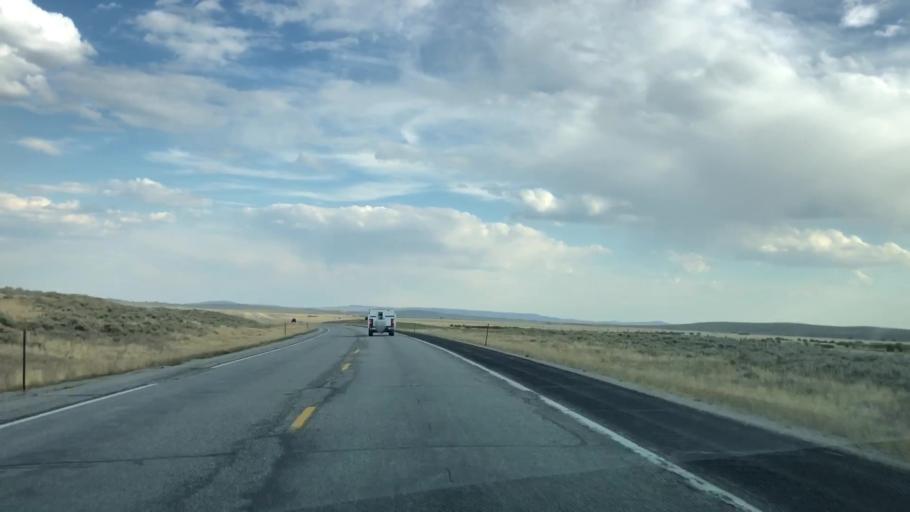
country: US
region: Wyoming
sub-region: Sublette County
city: Pinedale
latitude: 43.0480
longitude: -110.1490
